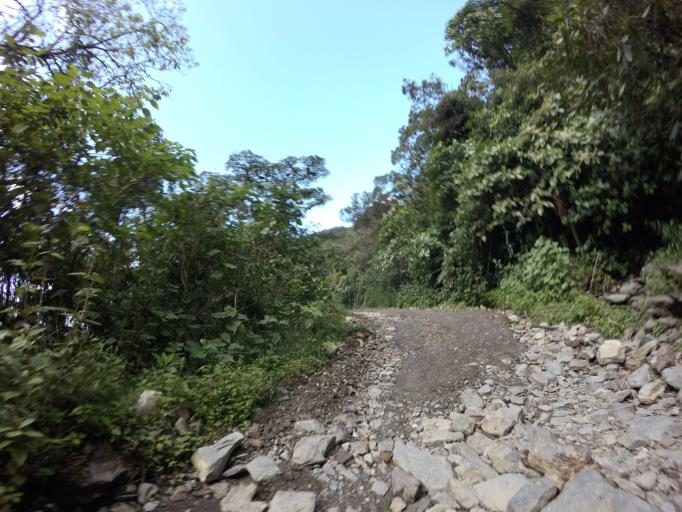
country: CO
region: Caldas
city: Pensilvania
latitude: 5.4500
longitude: -75.1511
